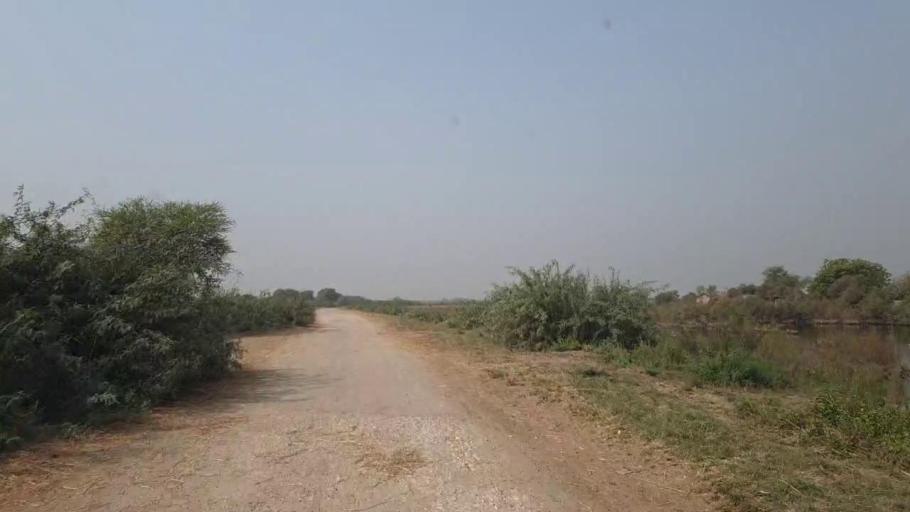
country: PK
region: Sindh
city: Matli
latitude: 25.1234
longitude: 68.6562
